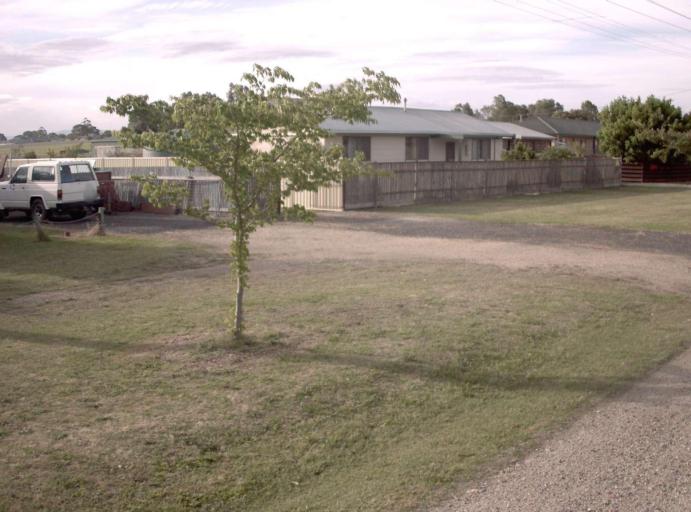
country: AU
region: Victoria
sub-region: Wellington
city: Sale
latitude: -37.9551
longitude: 146.9872
